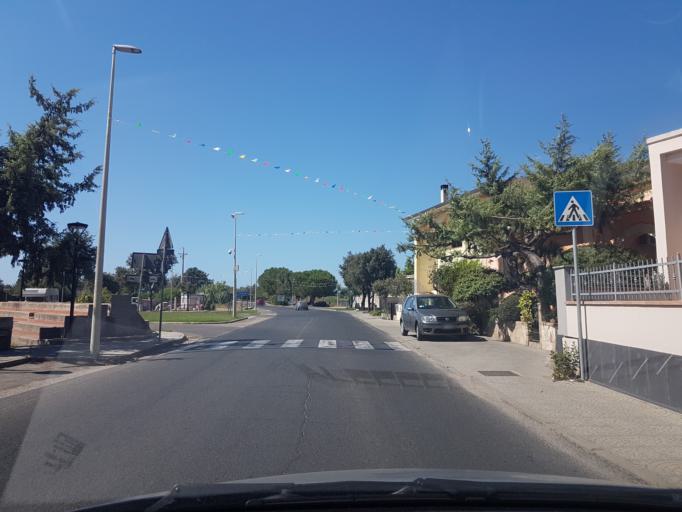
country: IT
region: Sardinia
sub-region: Provincia di Oristano
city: Riola Sardo
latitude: 39.9971
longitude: 8.5386
